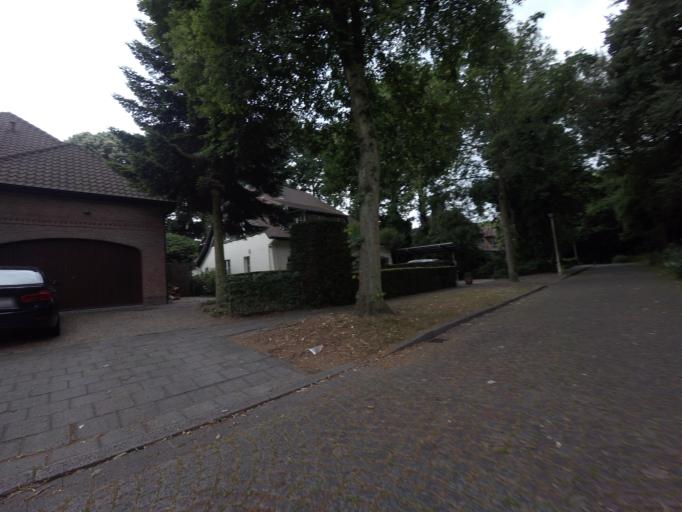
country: BE
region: Flanders
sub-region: Provincie Antwerpen
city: Edegem
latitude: 51.1714
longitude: 4.4177
